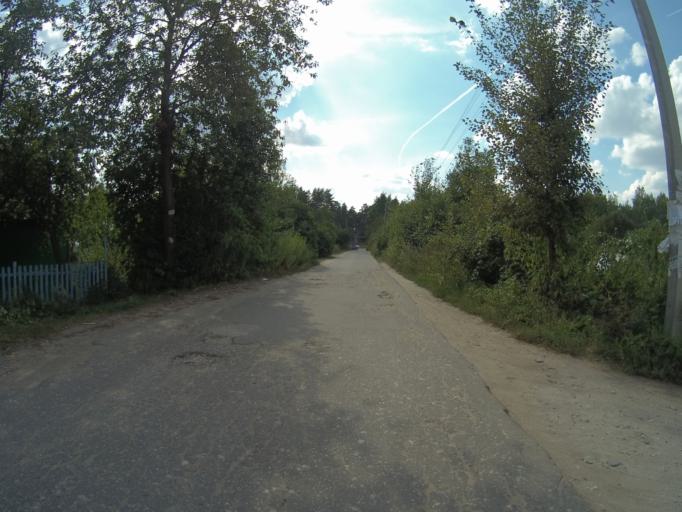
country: RU
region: Vladimir
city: Kommunar
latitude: 56.0488
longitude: 40.4404
